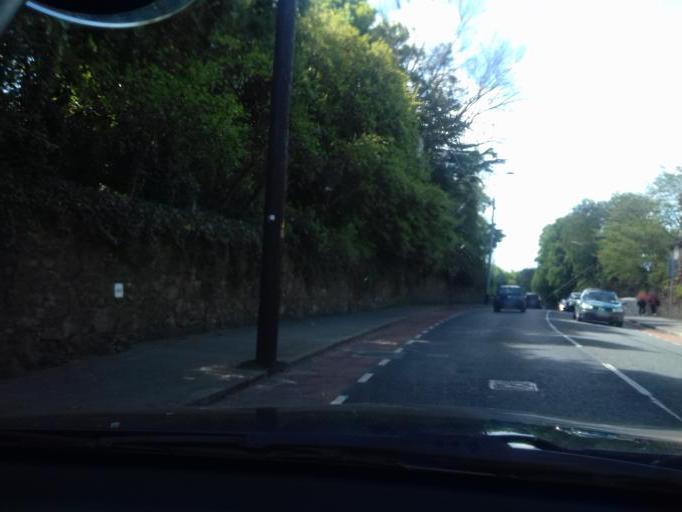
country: IE
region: Munster
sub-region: Waterford
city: Waterford
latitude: 52.2495
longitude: -7.0914
